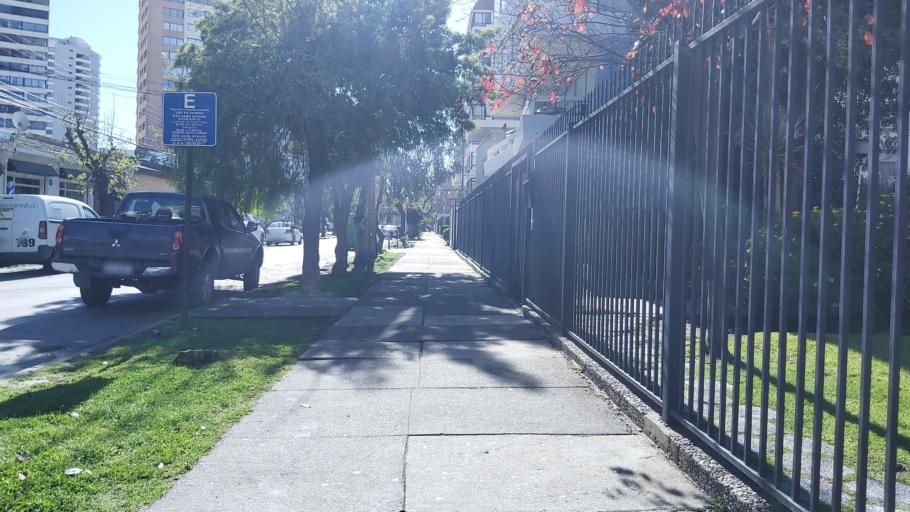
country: CL
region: Valparaiso
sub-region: Provincia de Valparaiso
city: Vina del Mar
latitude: -33.0164
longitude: -71.5540
